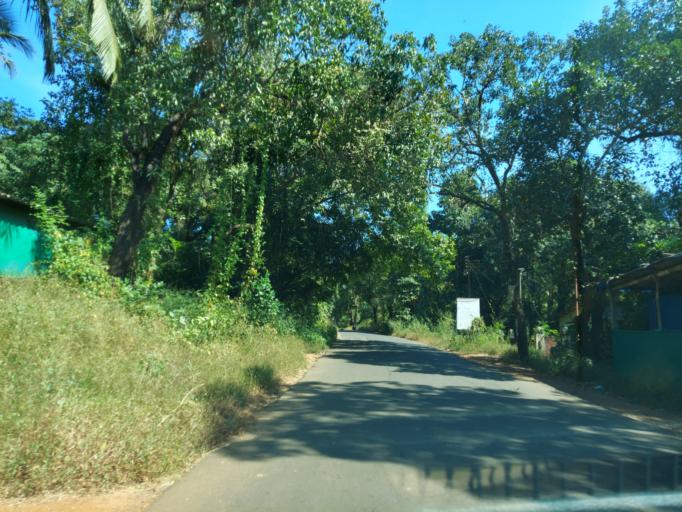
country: IN
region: Maharashtra
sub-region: Sindhudurg
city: Kudal
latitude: 15.9884
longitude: 73.6807
